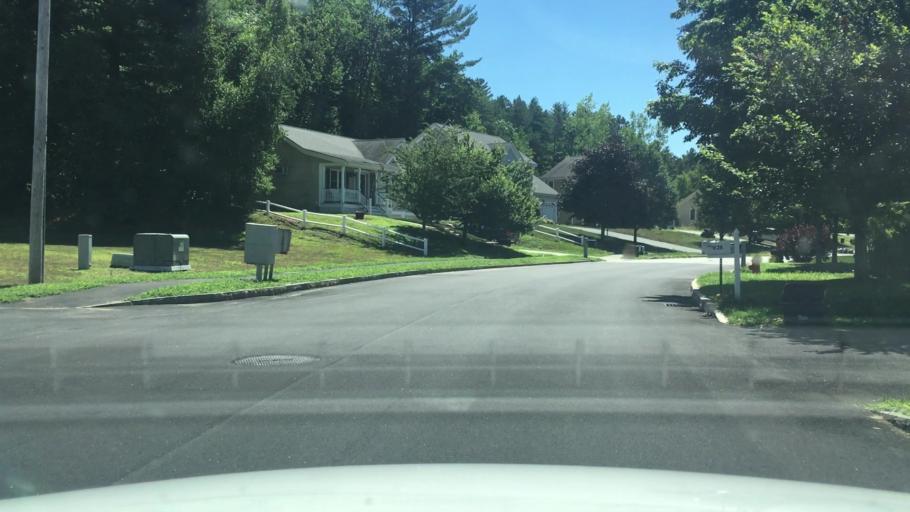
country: US
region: New Hampshire
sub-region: Merrimack County
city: Boscawen
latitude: 43.2727
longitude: -71.6001
